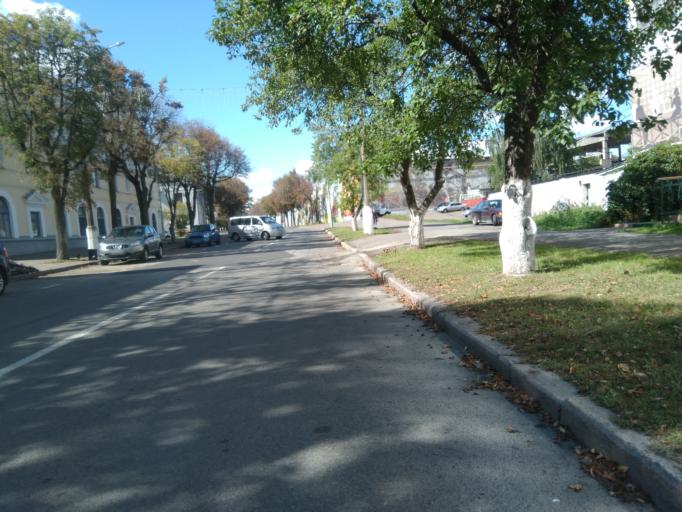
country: BY
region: Minsk
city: Minsk
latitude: 53.8952
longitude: 27.5756
